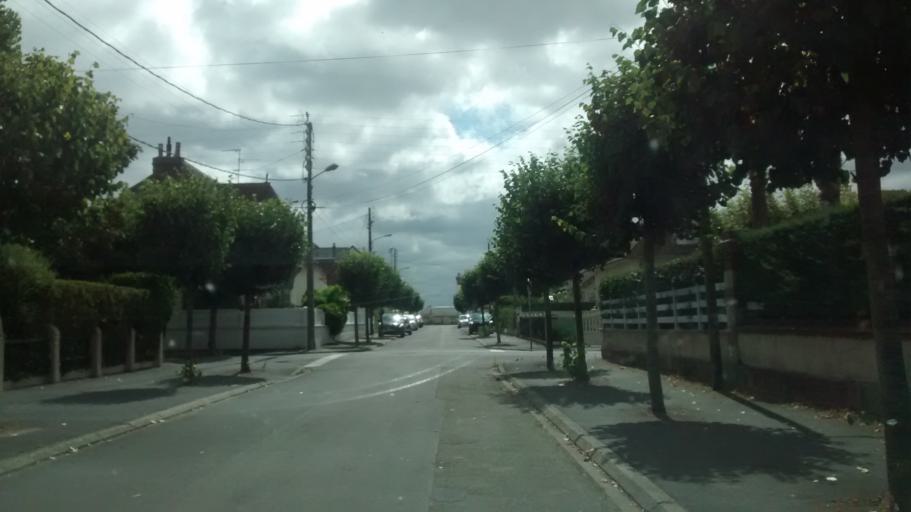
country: FR
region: Lower Normandy
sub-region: Departement du Calvados
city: Ouistreham
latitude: 49.2836
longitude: -0.2555
